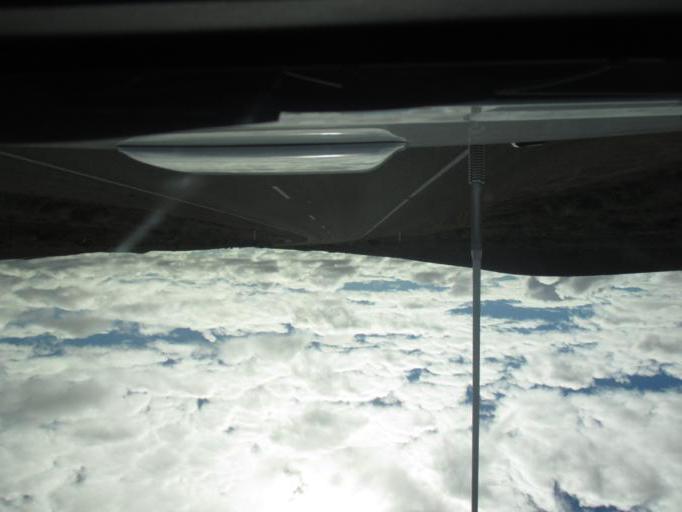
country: AU
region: South Australia
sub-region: Flinders Ranges
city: Quorn
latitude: -32.2603
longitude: 138.5053
